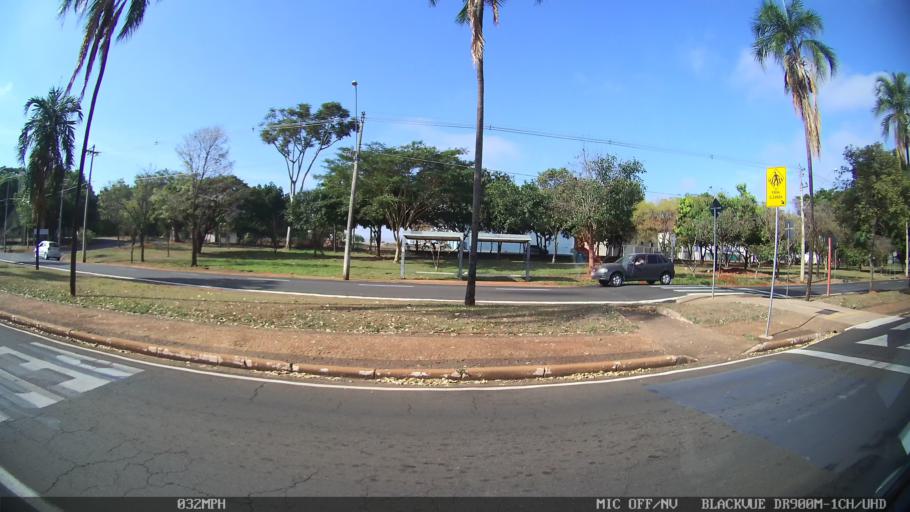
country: BR
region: Sao Paulo
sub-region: Sao Jose Do Rio Preto
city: Sao Jose do Rio Preto
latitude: -20.8137
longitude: -49.4082
